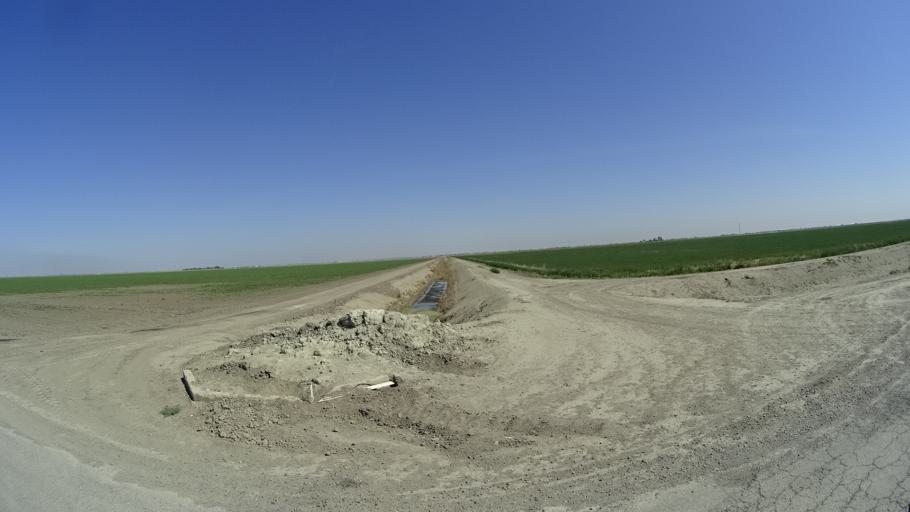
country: US
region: California
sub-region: Kings County
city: Corcoran
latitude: 36.0072
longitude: -119.5540
